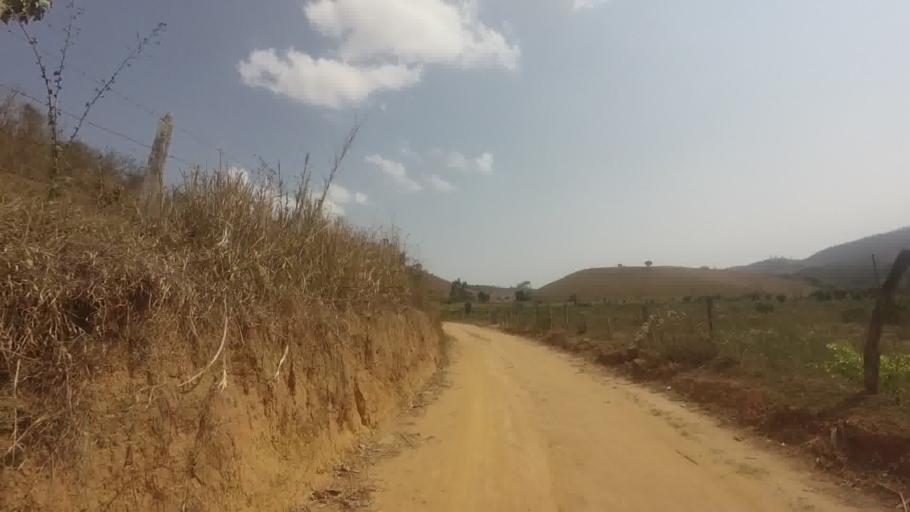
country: BR
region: Espirito Santo
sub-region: Sao Jose Do Calcado
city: Sao Jose do Calcado
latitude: -21.0315
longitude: -41.5188
